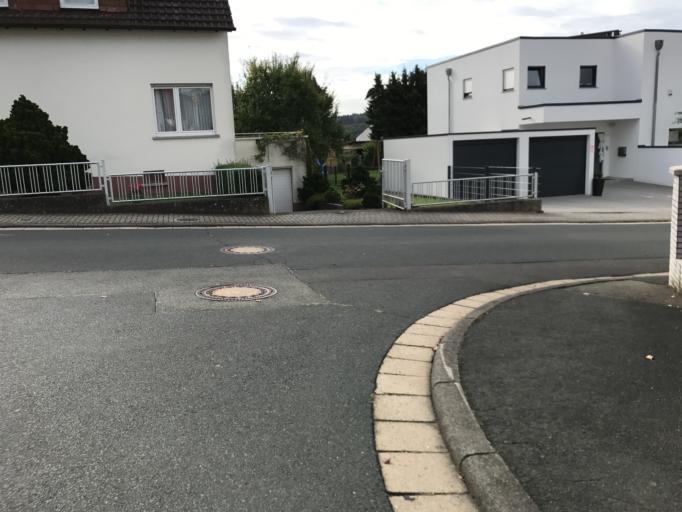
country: DE
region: Hesse
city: Weilburg
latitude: 50.4804
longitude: 8.2461
